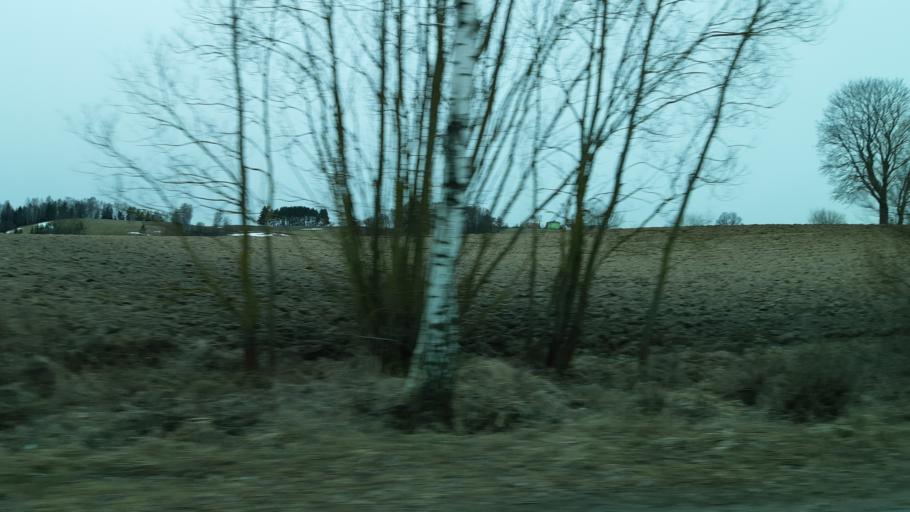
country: PL
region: Podlasie
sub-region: Suwalki
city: Suwalki
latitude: 54.3313
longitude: 22.9477
